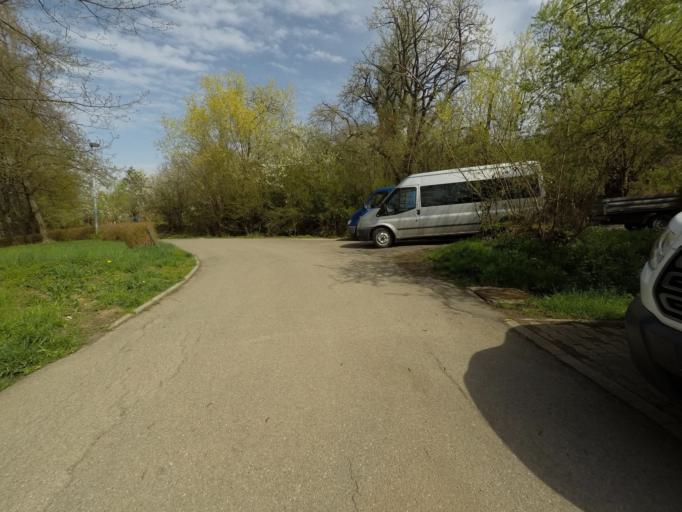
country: DE
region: Baden-Wuerttemberg
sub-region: Tuebingen Region
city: Reutlingen
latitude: 48.4723
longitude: 9.1993
